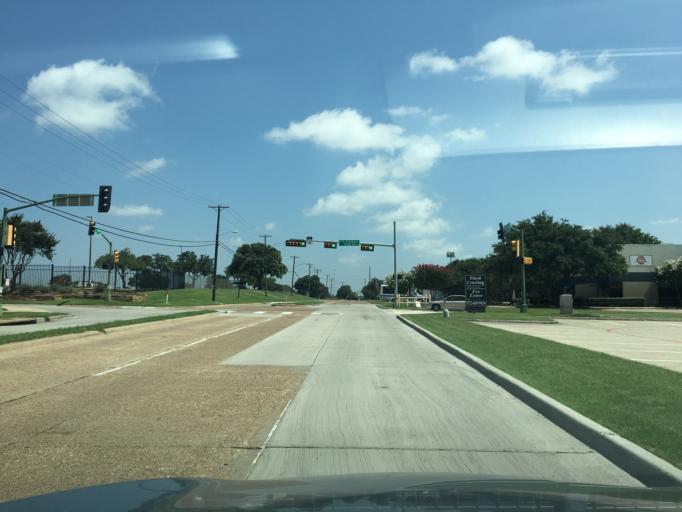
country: US
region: Texas
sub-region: Dallas County
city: Richardson
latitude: 32.9307
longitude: -96.7488
